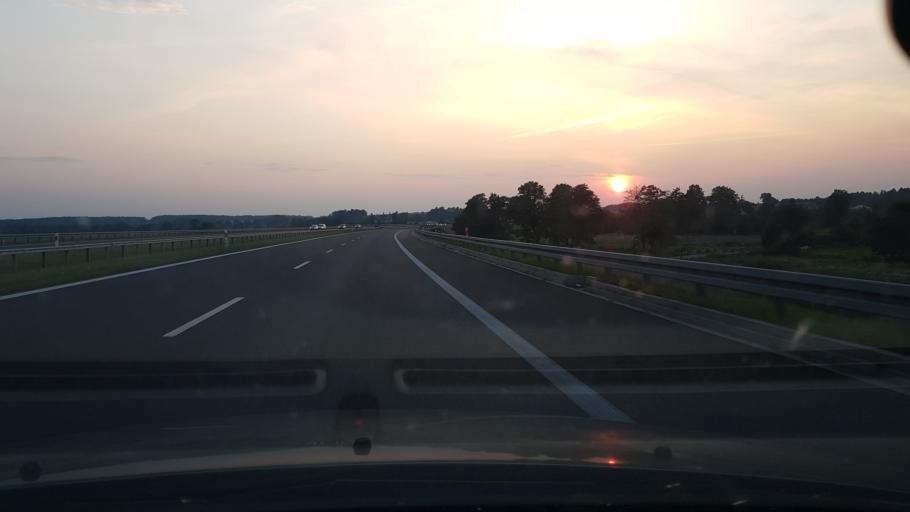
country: PL
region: Warmian-Masurian Voivodeship
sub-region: Powiat nidzicki
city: Nidzica
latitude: 53.3404
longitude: 20.4122
